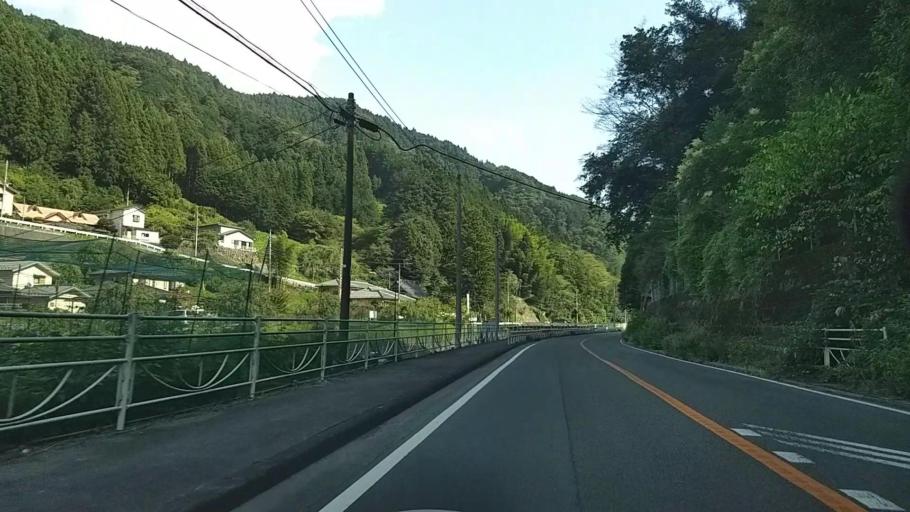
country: JP
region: Shizuoka
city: Fujinomiya
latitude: 35.3487
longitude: 138.4223
